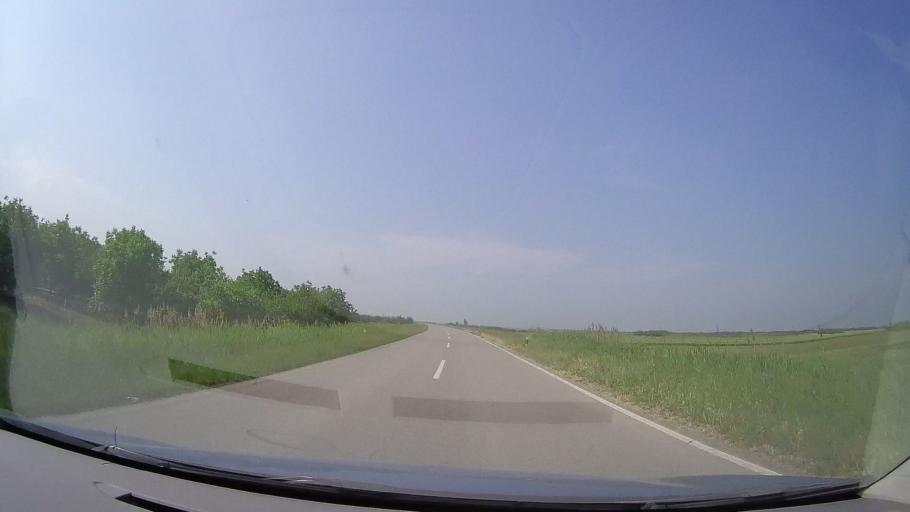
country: RS
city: Jasa Tomic
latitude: 45.4308
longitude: 20.8402
